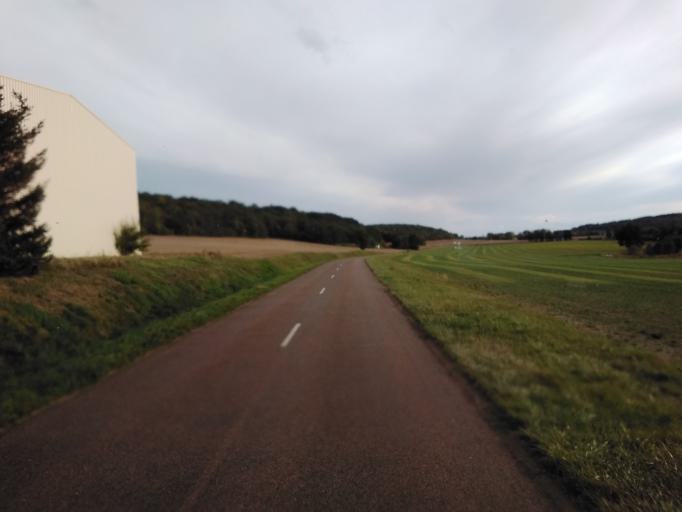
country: FR
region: Champagne-Ardenne
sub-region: Departement de l'Aube
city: Les Riceys
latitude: 47.9135
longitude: 4.3650
